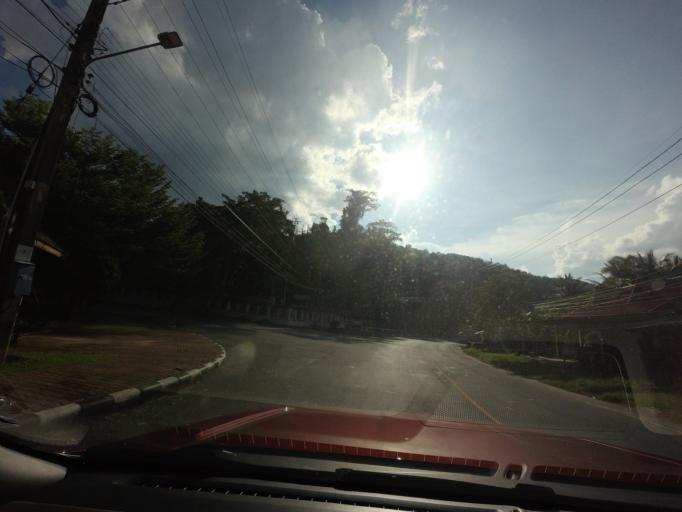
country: TH
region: Yala
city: Than To
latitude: 6.1614
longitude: 101.2703
